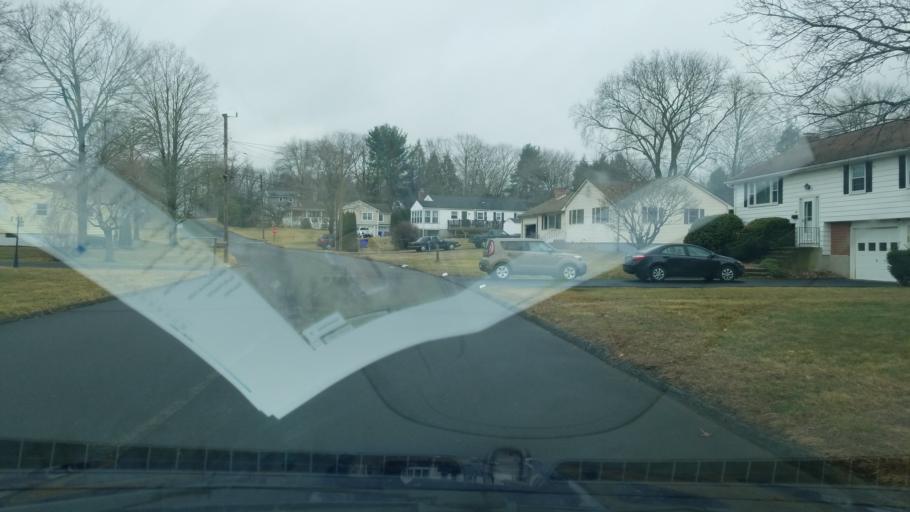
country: US
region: Connecticut
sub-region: Hartford County
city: Wethersfield
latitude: 41.6717
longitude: -72.6712
